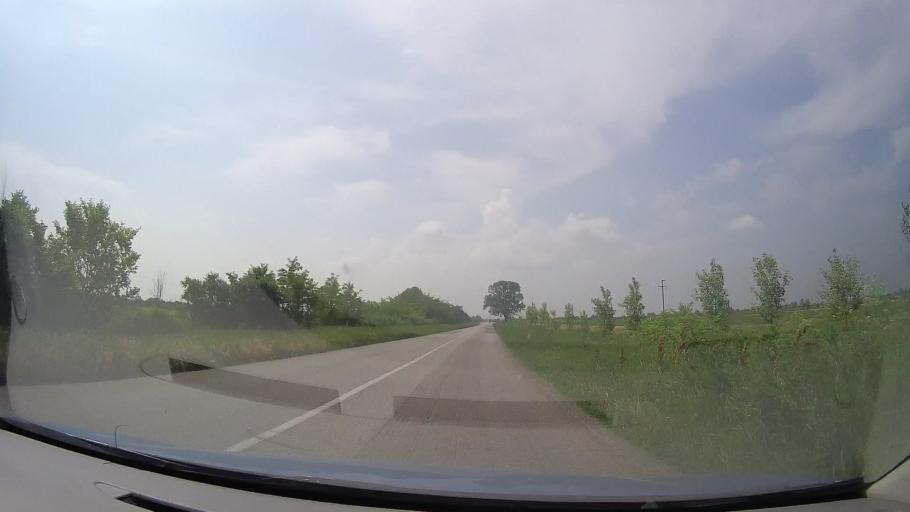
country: RS
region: Autonomna Pokrajina Vojvodina
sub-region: Juznobanatski Okrug
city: Kovacica
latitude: 45.0810
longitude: 20.6412
